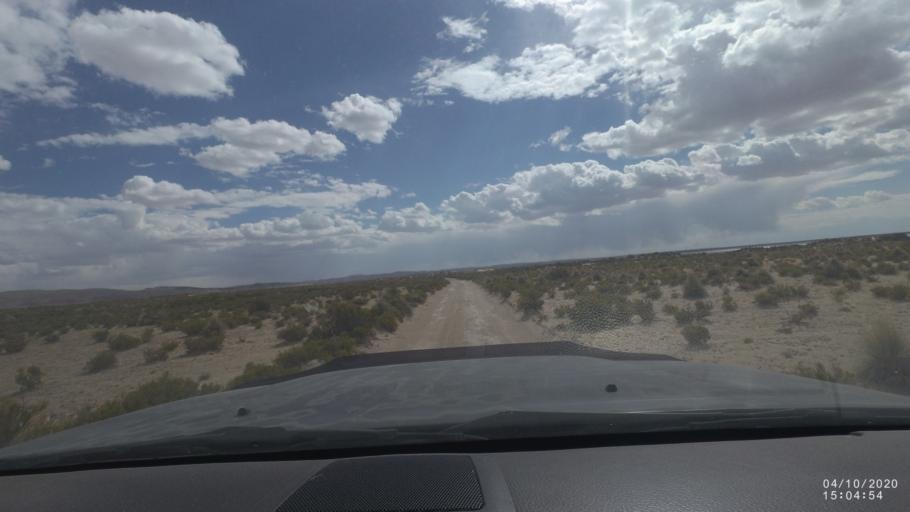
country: BO
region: Oruro
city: Poopo
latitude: -18.6910
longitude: -67.5529
